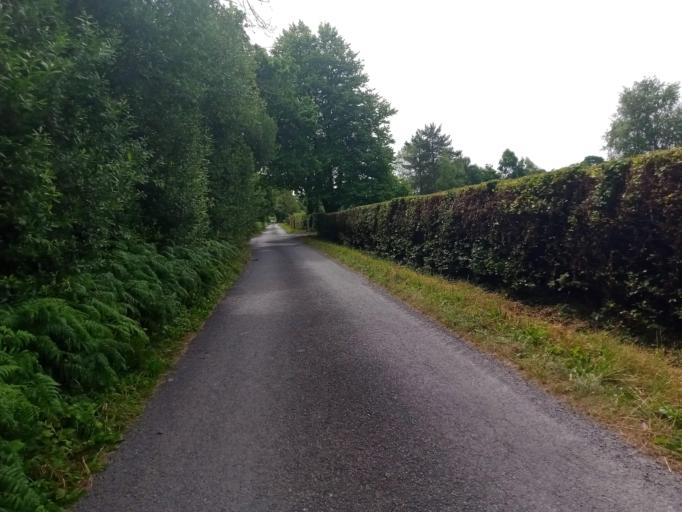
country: IE
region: Leinster
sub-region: Laois
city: Abbeyleix
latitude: 52.8818
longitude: -7.3552
